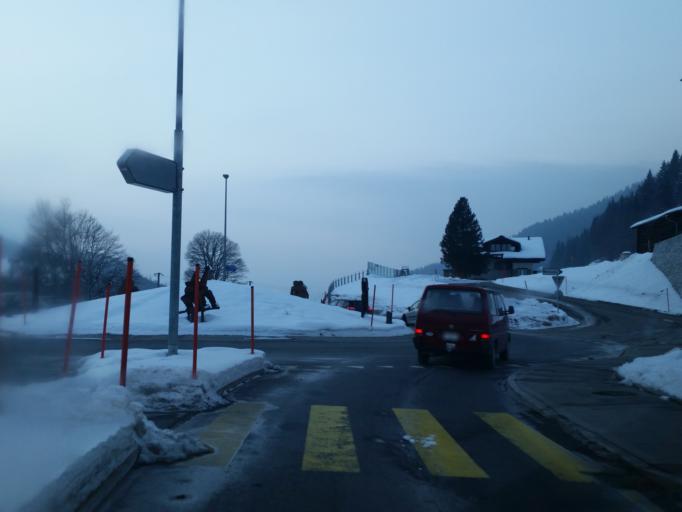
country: CH
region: Grisons
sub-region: Praettigau/Davos District
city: Klosters Serneus
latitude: 46.8942
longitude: 9.8431
